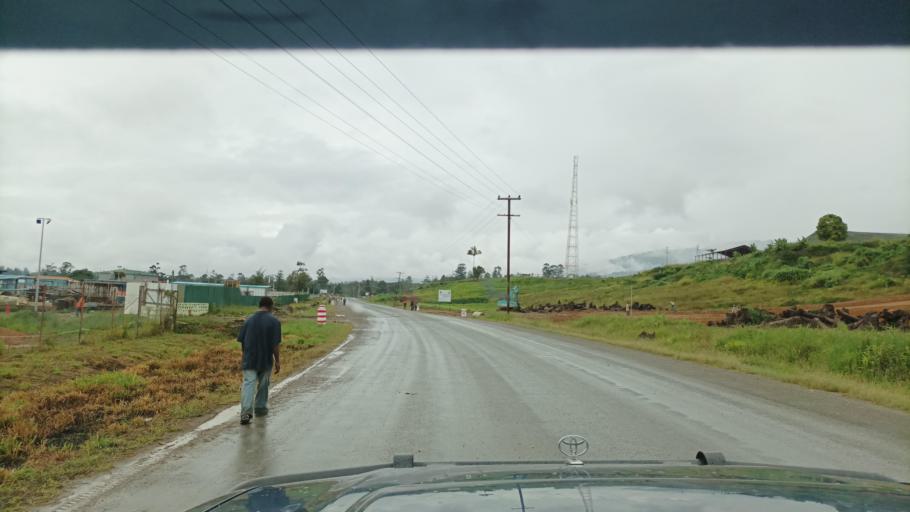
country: PG
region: Jiwaka
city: Minj
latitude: -5.8478
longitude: 144.6227
